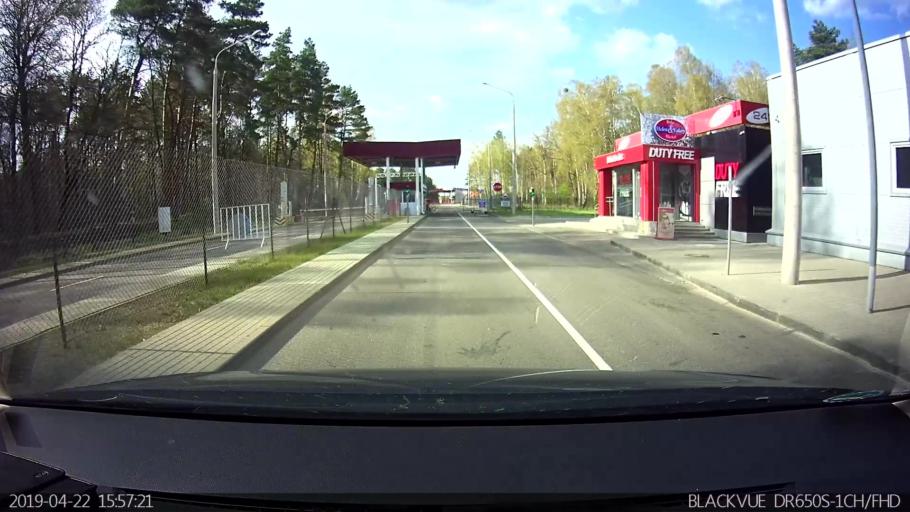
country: PL
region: Podlasie
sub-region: Powiat hajnowski
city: Czeremcha
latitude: 52.4688
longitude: 23.3590
